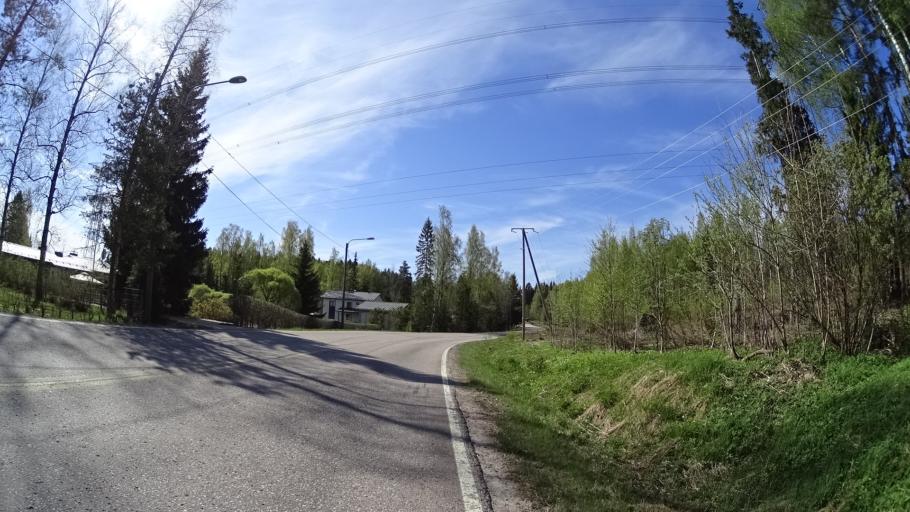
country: FI
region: Uusimaa
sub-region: Helsinki
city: Nurmijaervi
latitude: 60.3846
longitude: 24.8373
